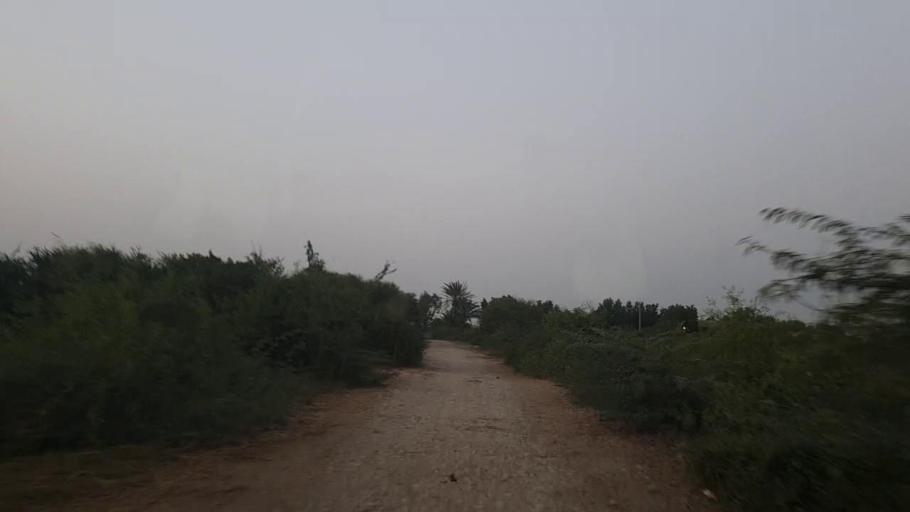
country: PK
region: Sindh
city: Mirpur Sakro
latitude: 24.5876
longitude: 67.7836
